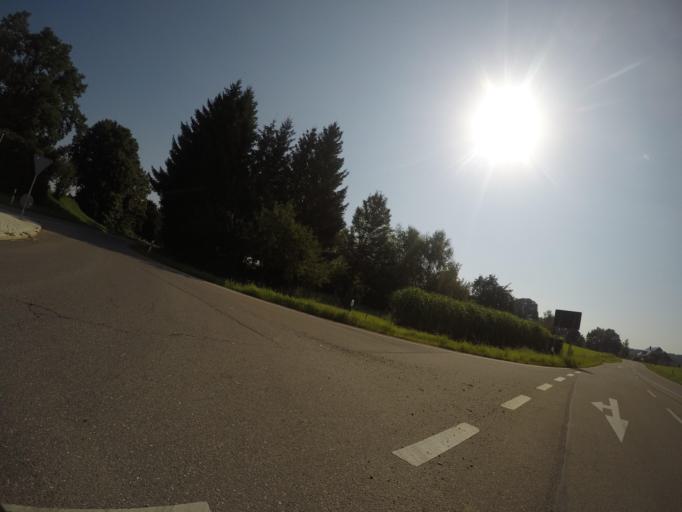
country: DE
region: Baden-Wuerttemberg
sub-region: Tuebingen Region
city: Wain
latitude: 48.1876
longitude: 10.0251
